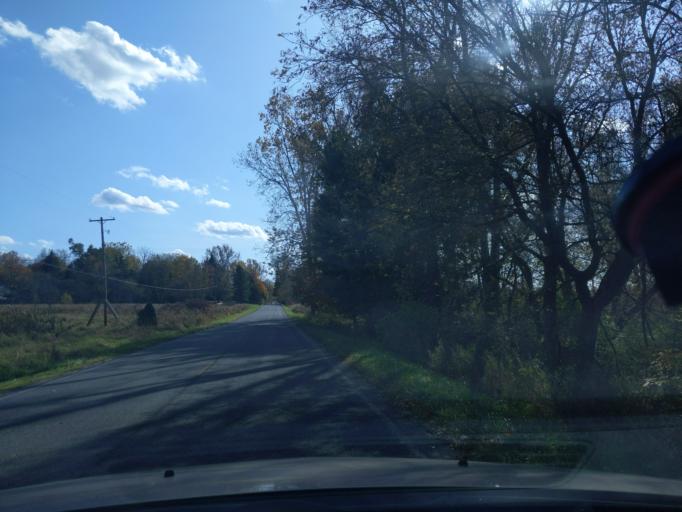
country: US
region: Michigan
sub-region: Ingham County
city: Haslett
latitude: 42.7416
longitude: -84.3931
